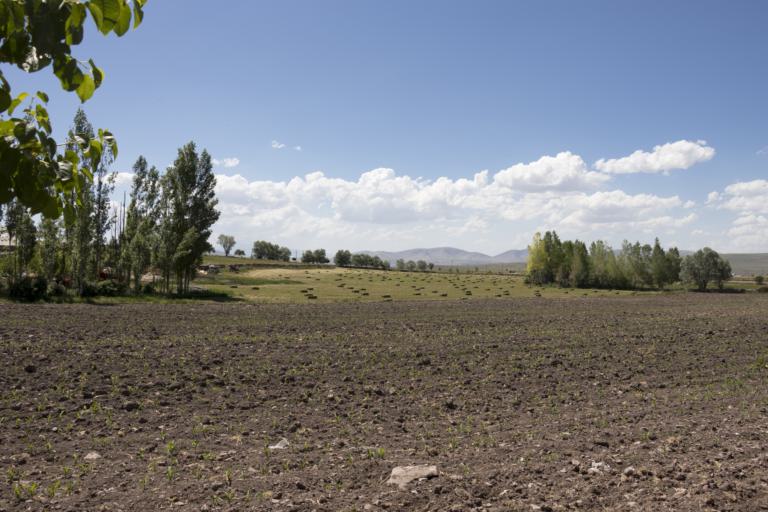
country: TR
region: Kayseri
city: Toklar
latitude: 38.4235
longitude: 36.0966
